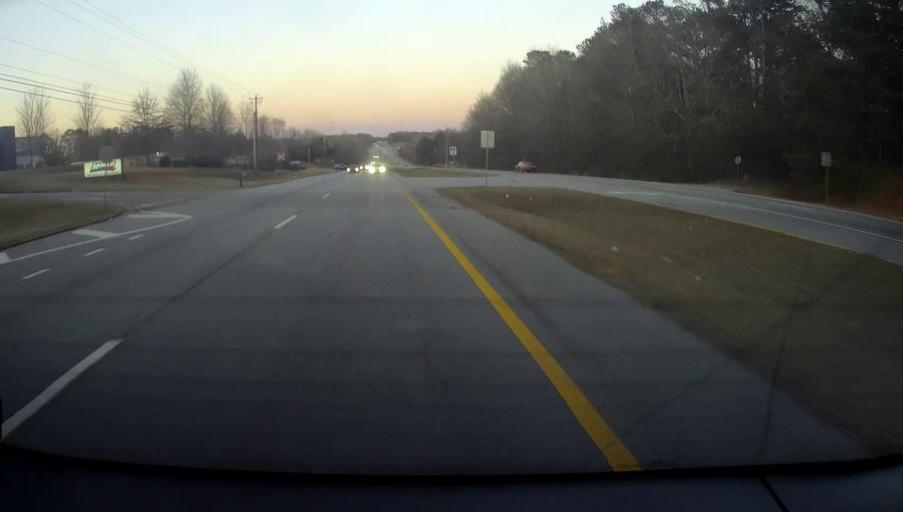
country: US
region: Georgia
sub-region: Fayette County
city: Fayetteville
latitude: 33.4888
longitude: -84.4328
